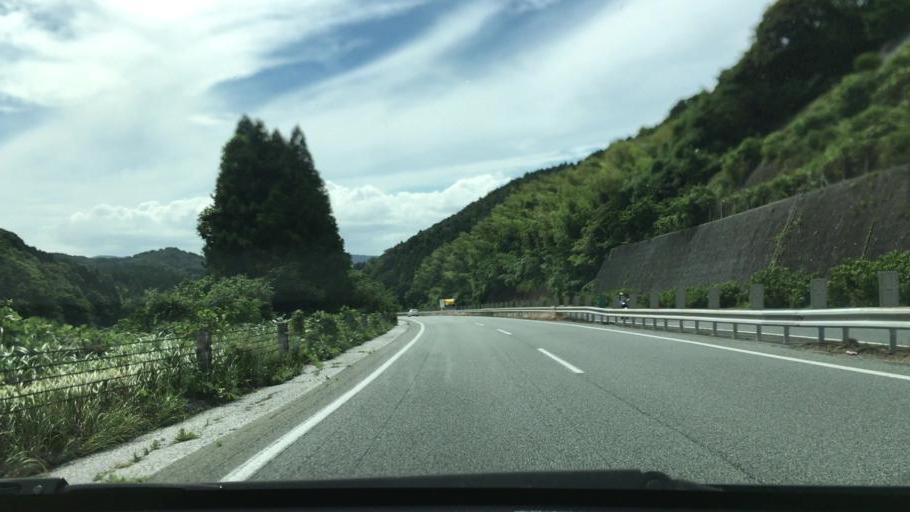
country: JP
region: Yamaguchi
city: Ogori-shimogo
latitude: 34.1428
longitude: 131.3574
